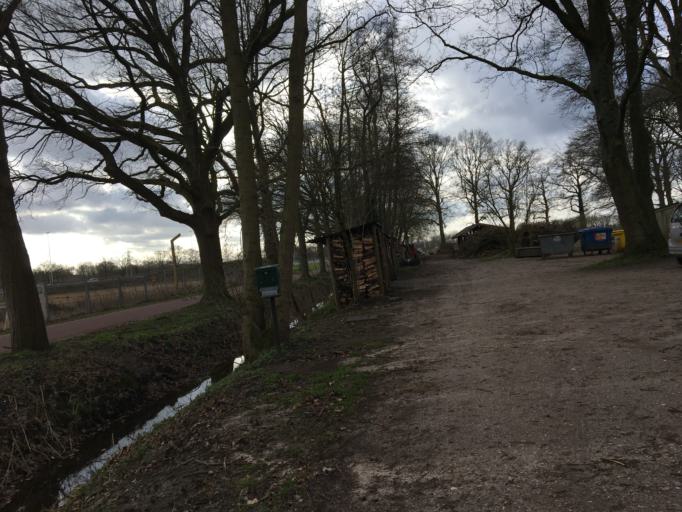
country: NL
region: Utrecht
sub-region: Gemeente Utrechtse Heuvelrug
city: Driebergen-Rijsenburg
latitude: 52.0606
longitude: 5.2599
